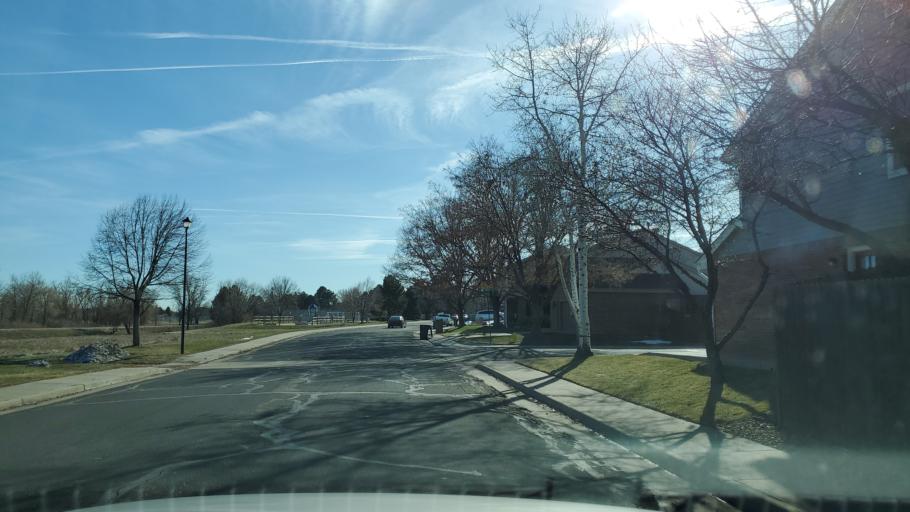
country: US
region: Colorado
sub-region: Adams County
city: Northglenn
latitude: 39.9235
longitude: -104.9534
